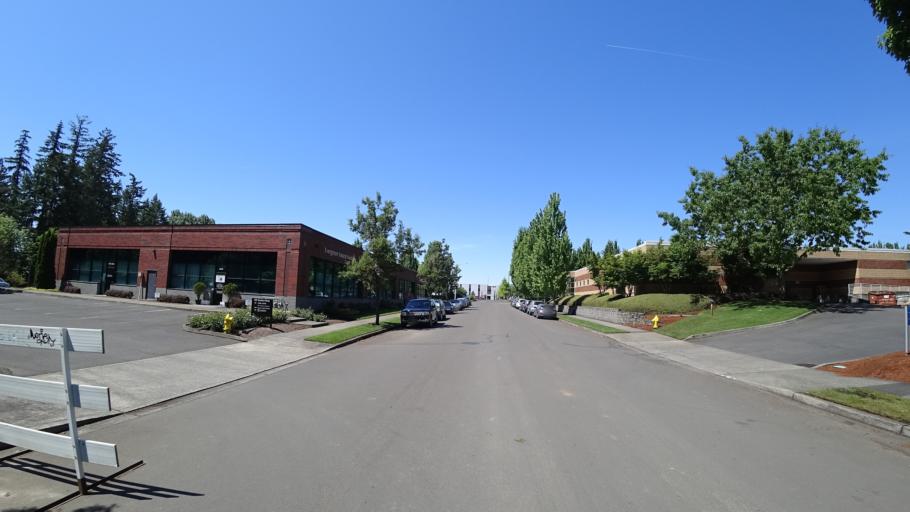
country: US
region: Oregon
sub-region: Washington County
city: Rockcreek
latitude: 45.5319
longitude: -122.9221
